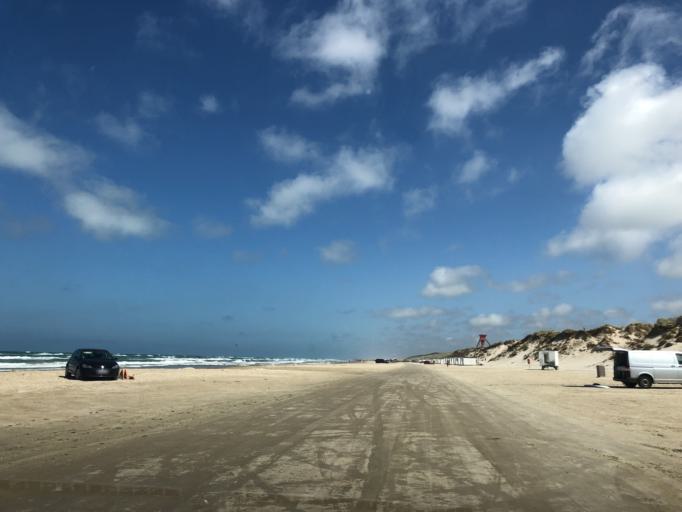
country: DK
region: North Denmark
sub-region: Jammerbugt Kommune
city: Pandrup
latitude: 57.2508
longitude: 9.5739
